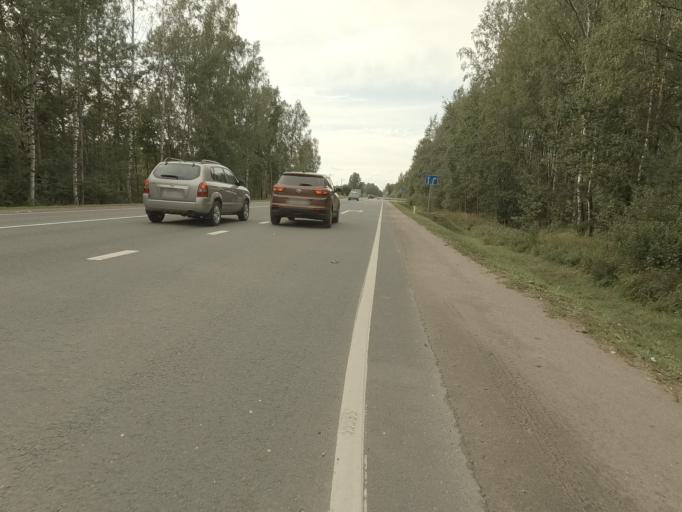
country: RU
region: Leningrad
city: Kirovsk
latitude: 59.8534
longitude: 31.0201
